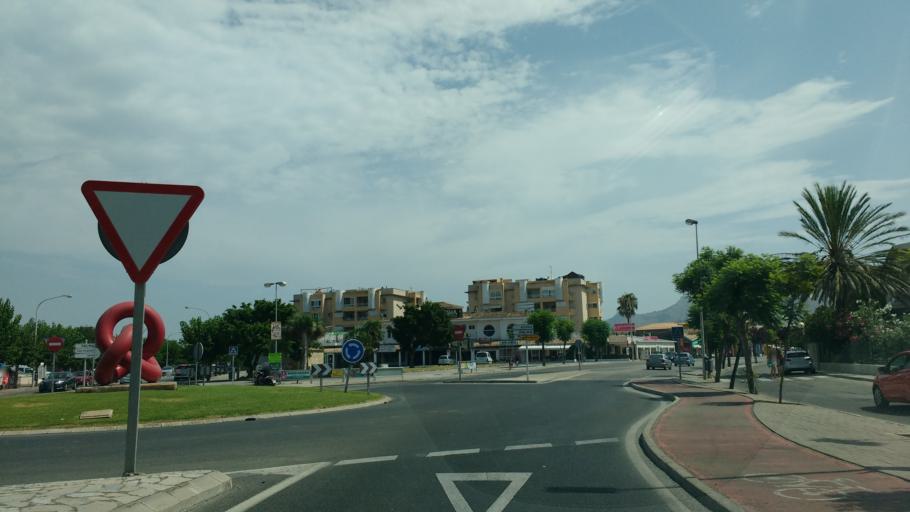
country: ES
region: Balearic Islands
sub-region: Illes Balears
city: Port d'Alcudia
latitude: 39.8395
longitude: 3.1210
